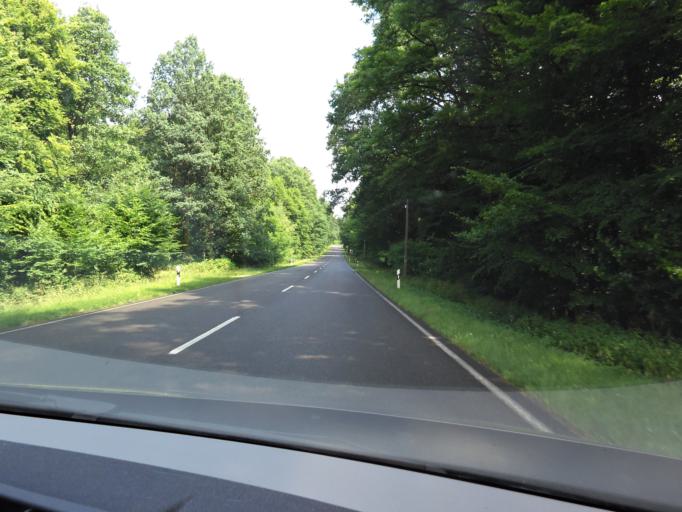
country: DE
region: Saxony
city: Bad Duben
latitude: 51.6644
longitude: 12.6000
